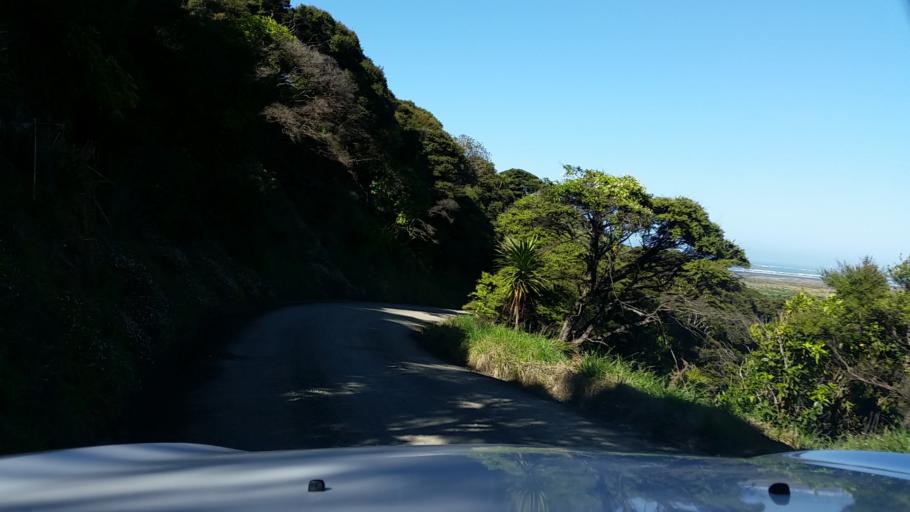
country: NZ
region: Auckland
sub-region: Auckland
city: Titirangi
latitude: -37.0342
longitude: 174.5160
